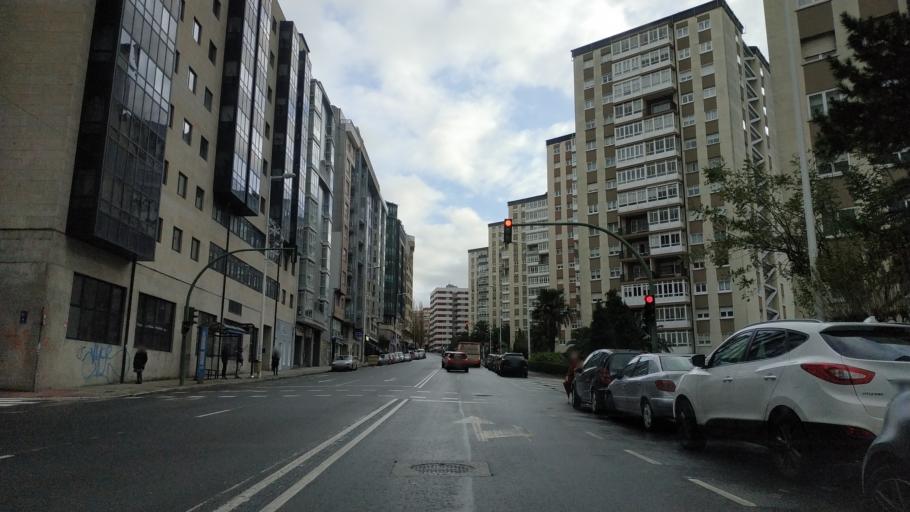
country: ES
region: Galicia
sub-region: Provincia da Coruna
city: A Coruna
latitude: 43.3495
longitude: -8.4037
